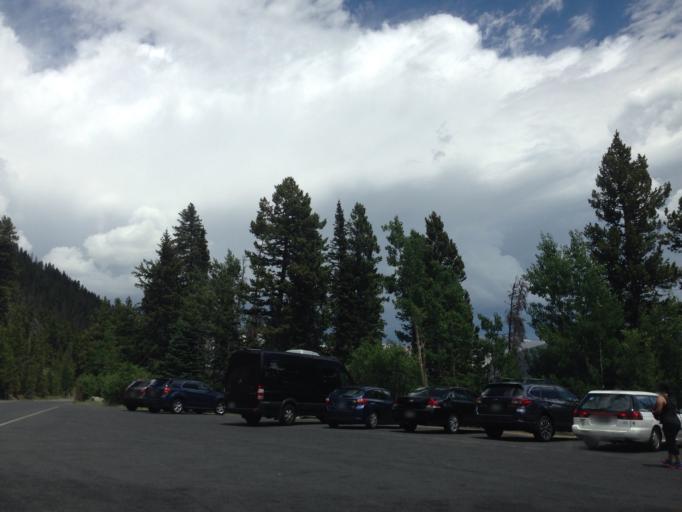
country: US
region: Colorado
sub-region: Larimer County
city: Estes Park
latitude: 40.3877
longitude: -105.6328
